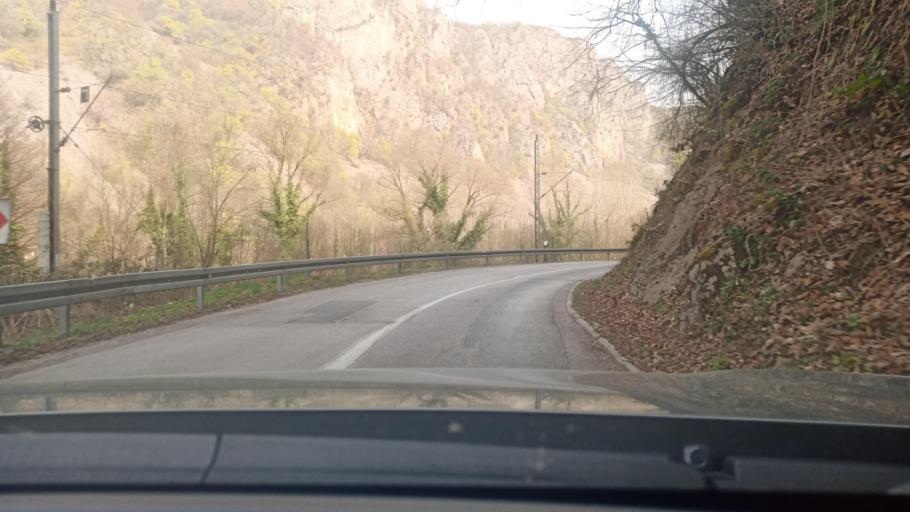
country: BA
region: Federation of Bosnia and Herzegovina
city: Stijena
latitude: 44.9036
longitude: 16.0277
